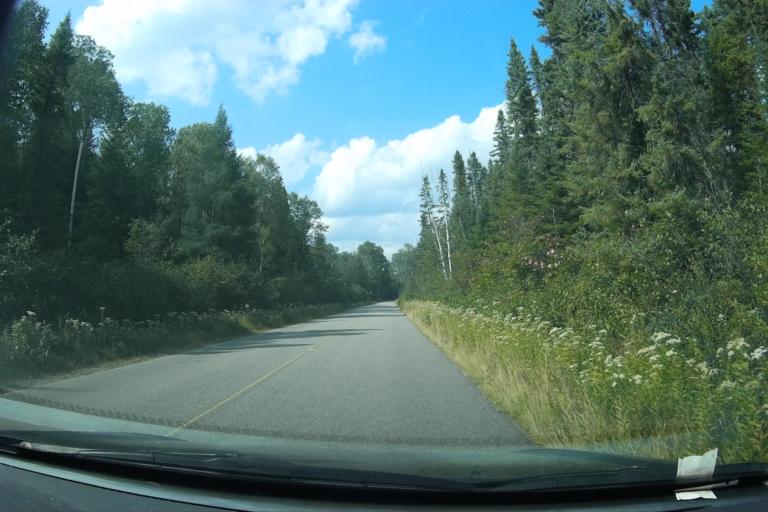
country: CA
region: Ontario
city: Bancroft
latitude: 45.6237
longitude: -78.3492
